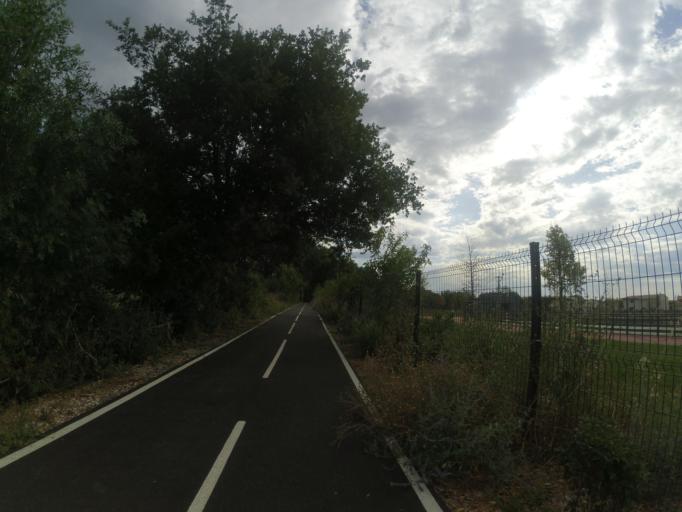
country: FR
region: Languedoc-Roussillon
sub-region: Departement des Pyrenees-Orientales
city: Toulouges
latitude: 42.6762
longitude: 2.8259
